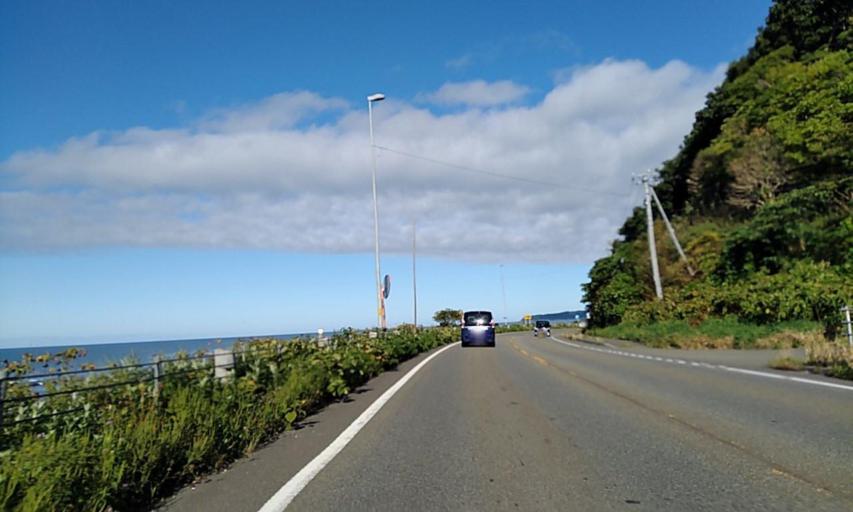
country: JP
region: Hokkaido
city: Shizunai-furukawacho
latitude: 42.2786
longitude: 142.4731
